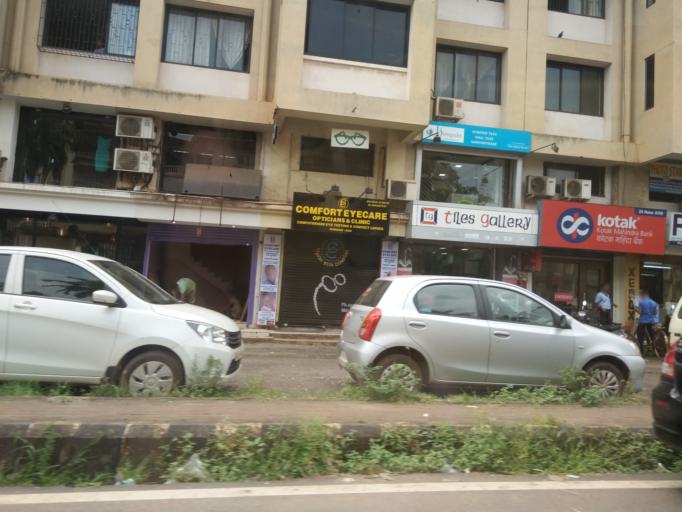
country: IN
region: Goa
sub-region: South Goa
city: Madgaon
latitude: 15.2592
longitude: 73.9652
